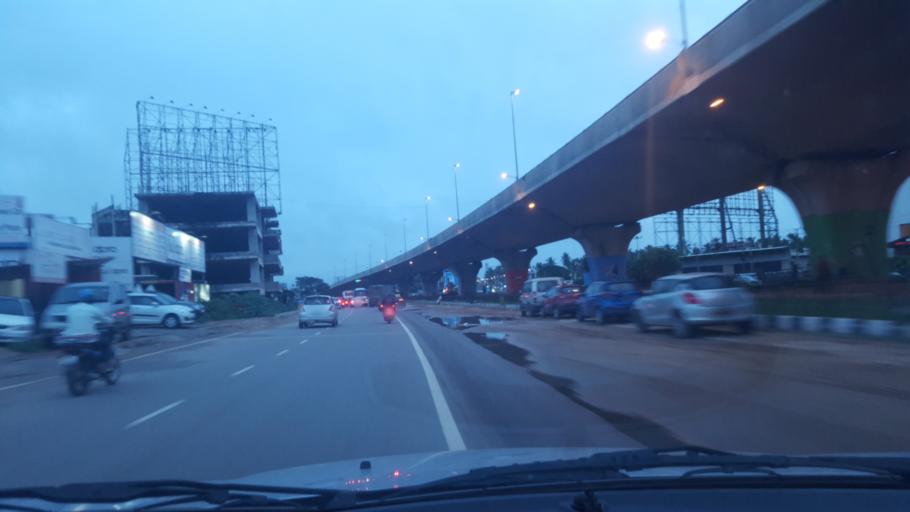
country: IN
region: Karnataka
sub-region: Bangalore Urban
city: Yelahanka
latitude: 13.1051
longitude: 77.6013
